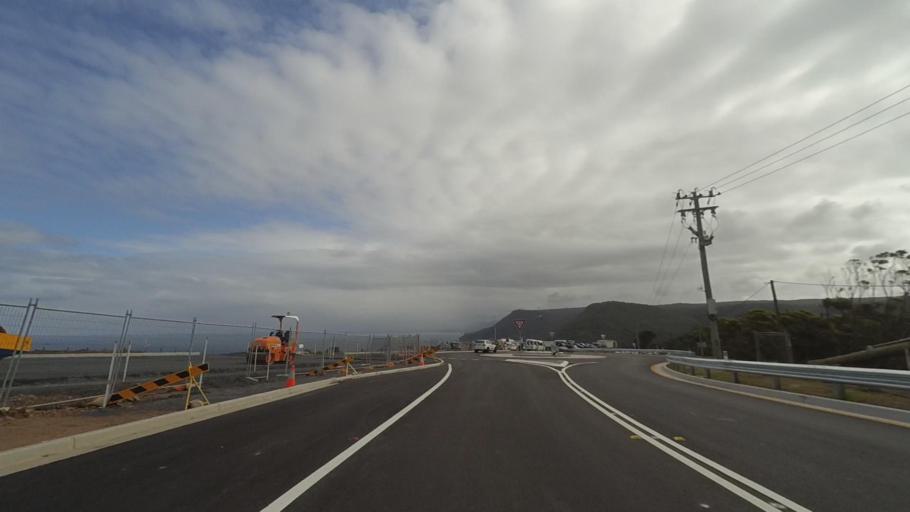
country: AU
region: New South Wales
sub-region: Wollongong
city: Helensburgh
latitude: -34.2230
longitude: 150.9980
